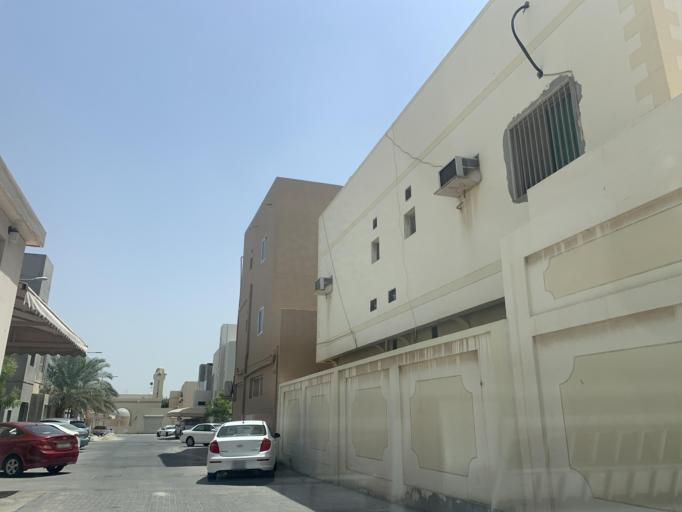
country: BH
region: Central Governorate
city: Madinat Hamad
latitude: 26.1456
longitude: 50.5039
